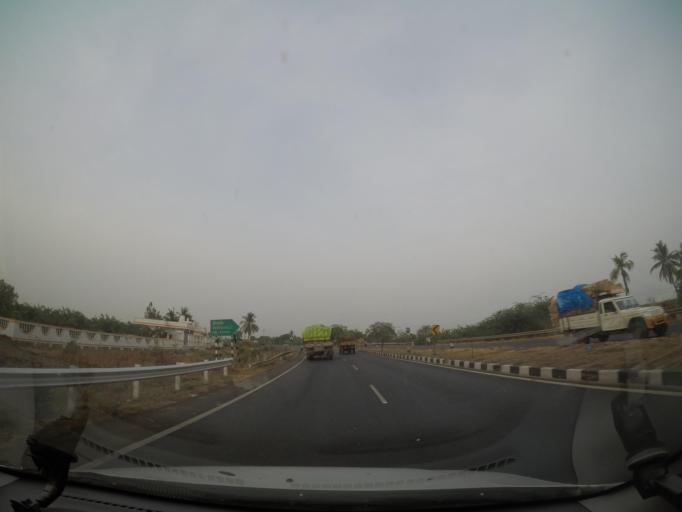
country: IN
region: Andhra Pradesh
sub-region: Krishna
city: Gannavaram
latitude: 16.6160
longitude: 80.9246
